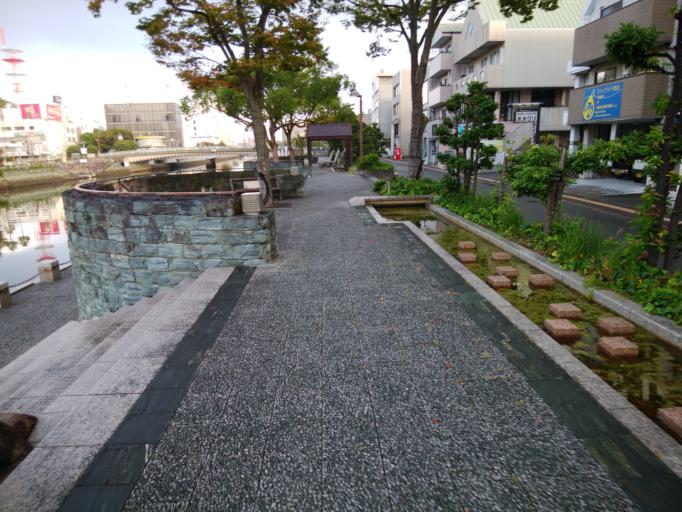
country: JP
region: Tokushima
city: Tokushima-shi
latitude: 34.0706
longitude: 134.5496
